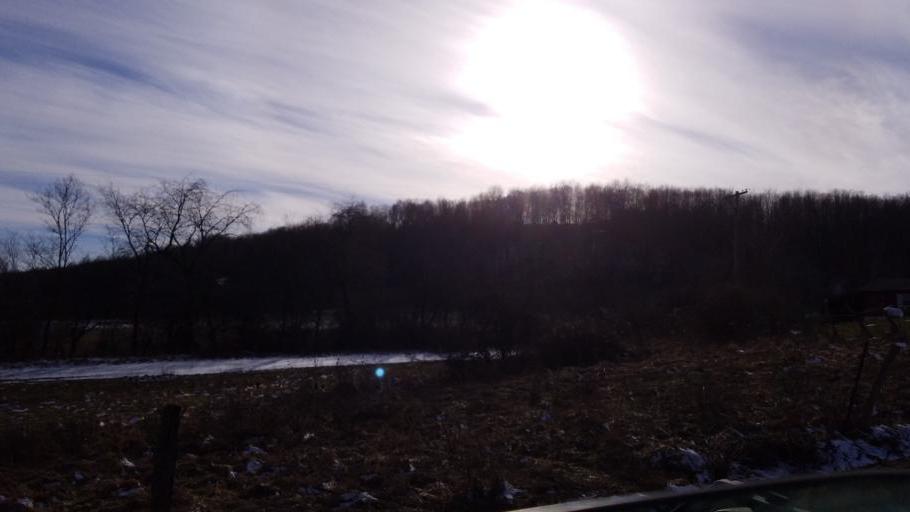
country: US
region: New York
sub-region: Allegany County
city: Andover
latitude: 42.1785
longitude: -77.8544
